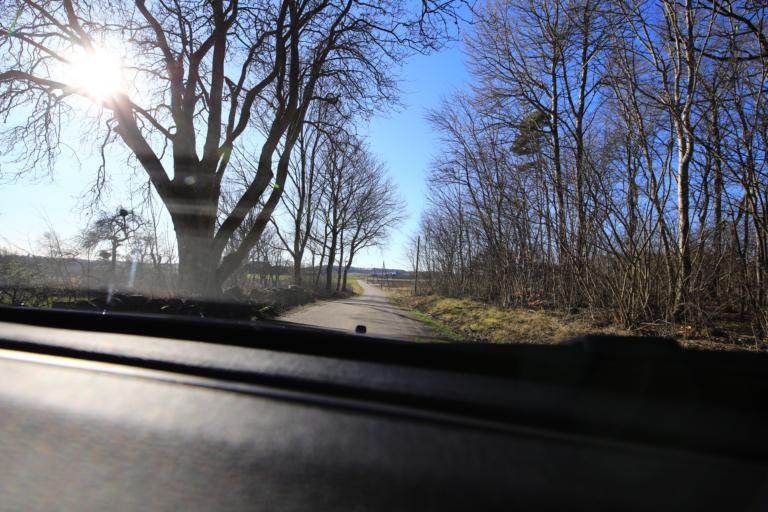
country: SE
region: Halland
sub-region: Varbergs Kommun
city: Tvaaker
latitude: 57.0635
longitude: 12.4215
